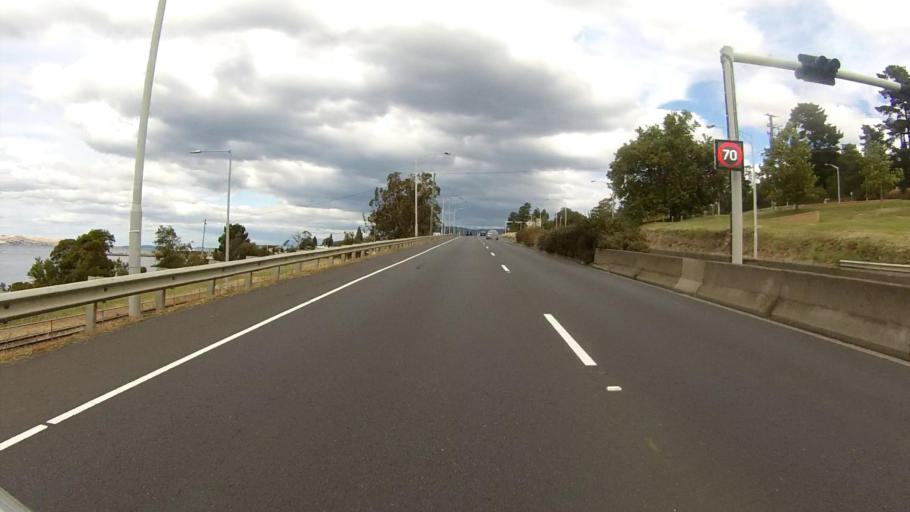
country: AU
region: Tasmania
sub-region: Hobart
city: Hobart
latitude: -42.8709
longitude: 147.3341
